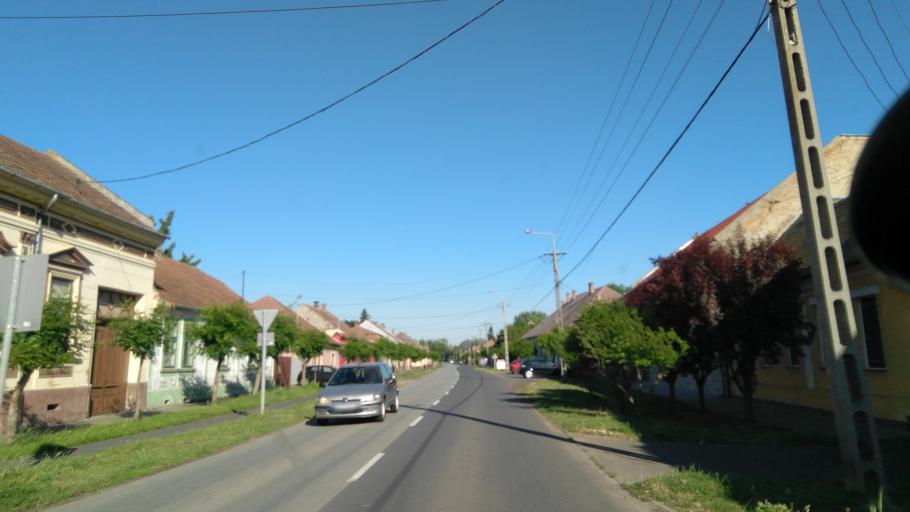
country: HU
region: Bekes
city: Elek
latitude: 46.5298
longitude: 21.2515
